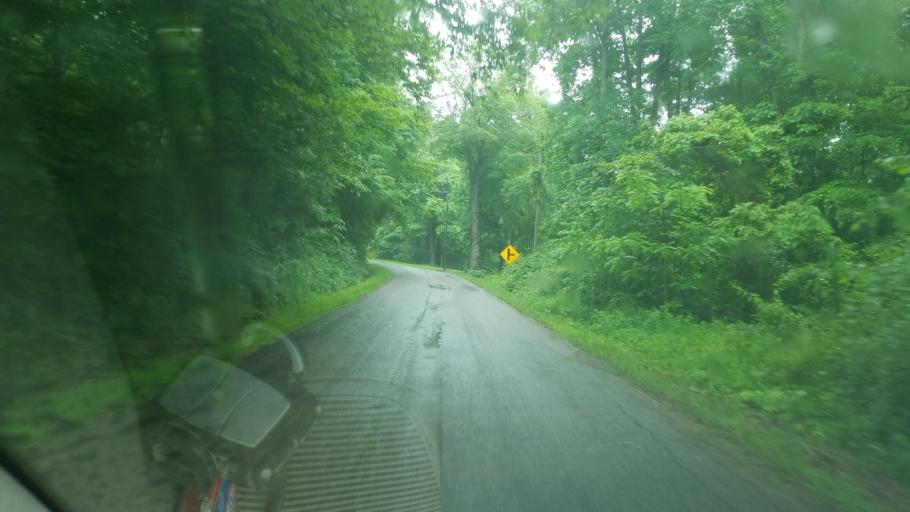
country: US
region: Ohio
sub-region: Sandusky County
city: Bellville
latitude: 40.6252
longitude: -82.4300
